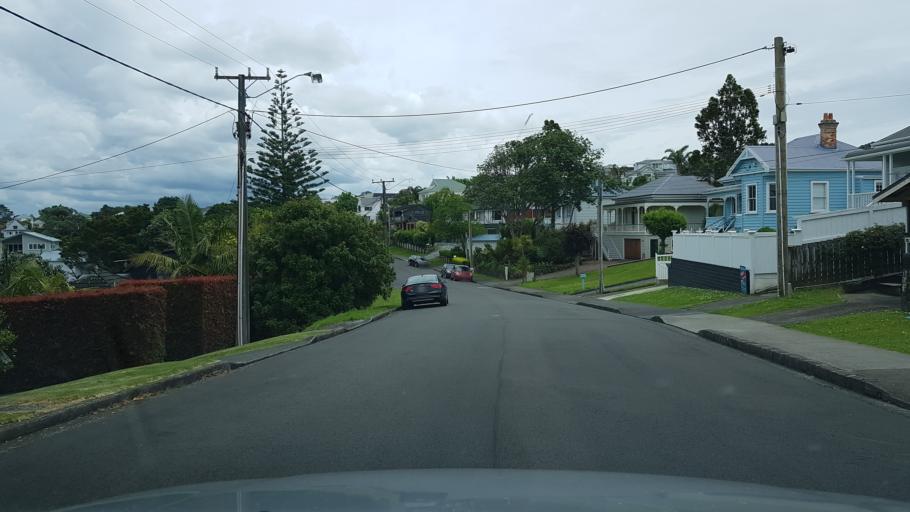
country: NZ
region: Auckland
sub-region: Auckland
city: North Shore
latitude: -36.8164
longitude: 174.7300
